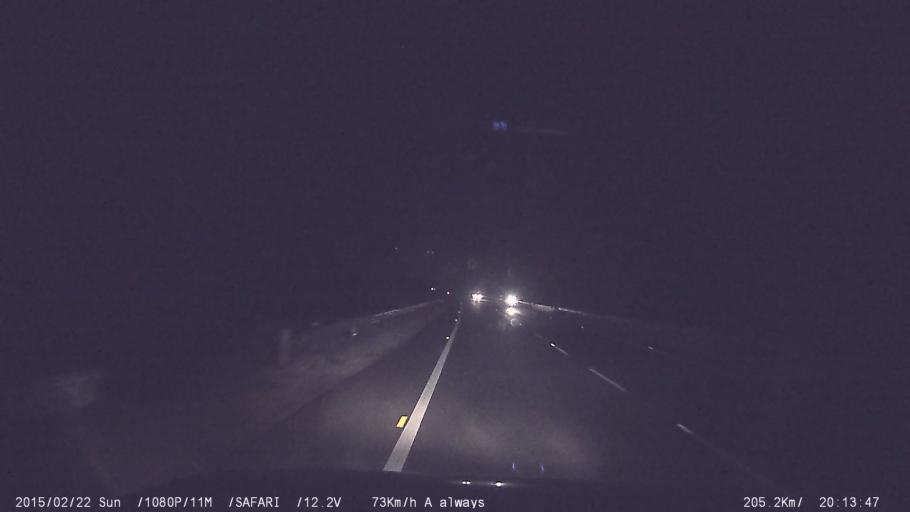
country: IN
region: Tamil Nadu
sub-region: Dindigul
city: Nilakottai
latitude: 10.2493
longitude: 77.8284
